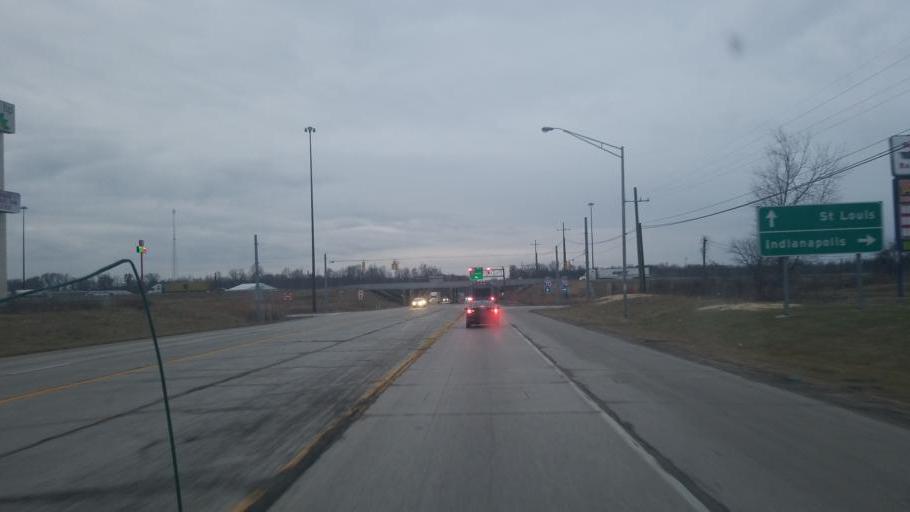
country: US
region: Indiana
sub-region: Clay County
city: Brazil
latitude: 39.4474
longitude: -87.1263
